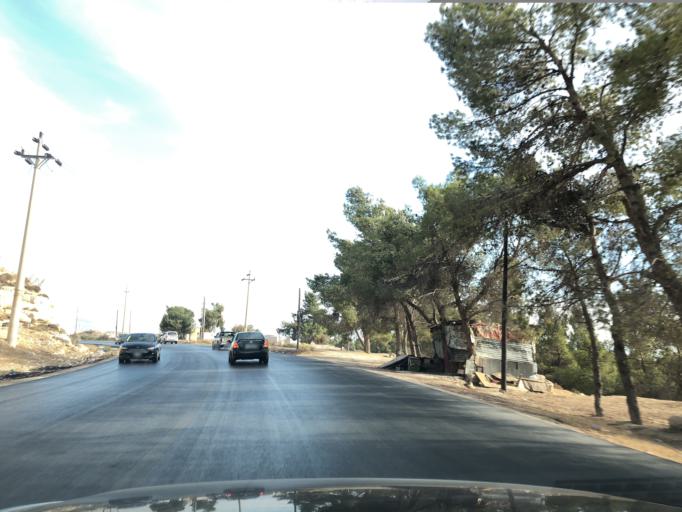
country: JO
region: Irbid
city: Al Kittah
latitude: 32.2819
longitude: 35.8593
